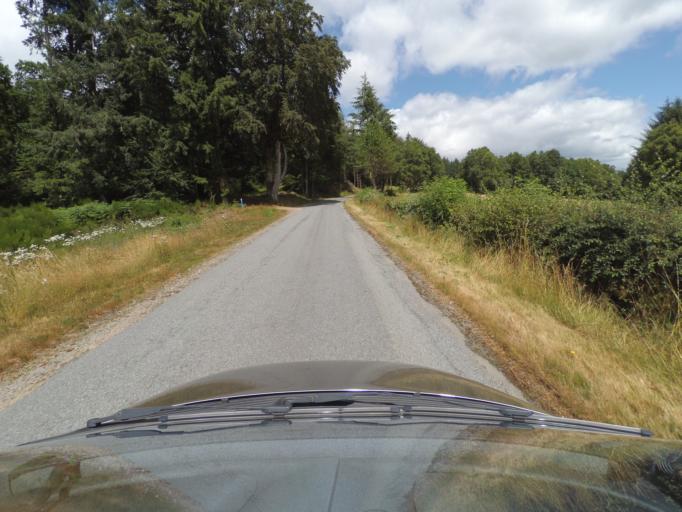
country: FR
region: Limousin
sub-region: Departement de la Creuse
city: Banize
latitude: 45.8008
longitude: 1.9310
